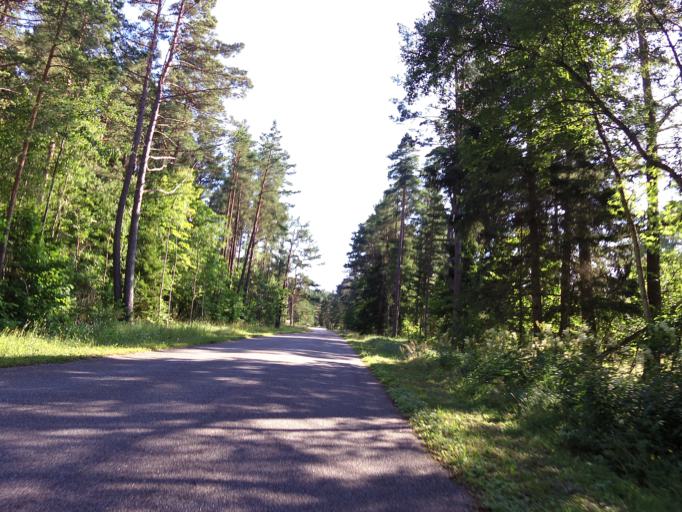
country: EE
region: Hiiumaa
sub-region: Kaerdla linn
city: Kardla
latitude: 58.8942
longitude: 22.2732
